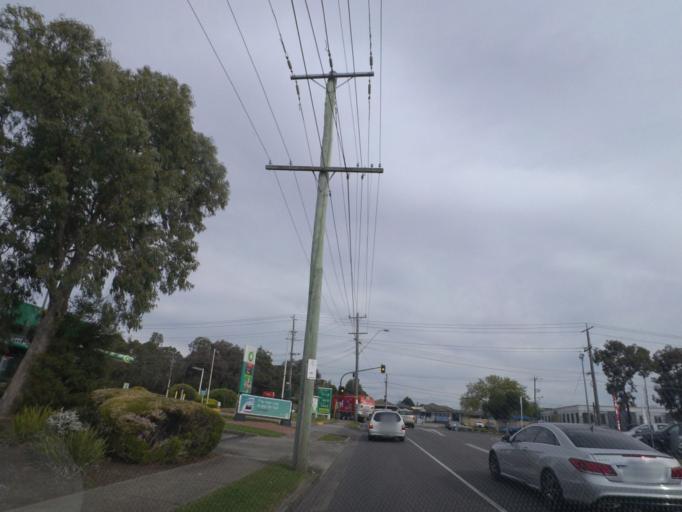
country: AU
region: Victoria
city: Forest Hill
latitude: -37.8360
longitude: 145.1884
